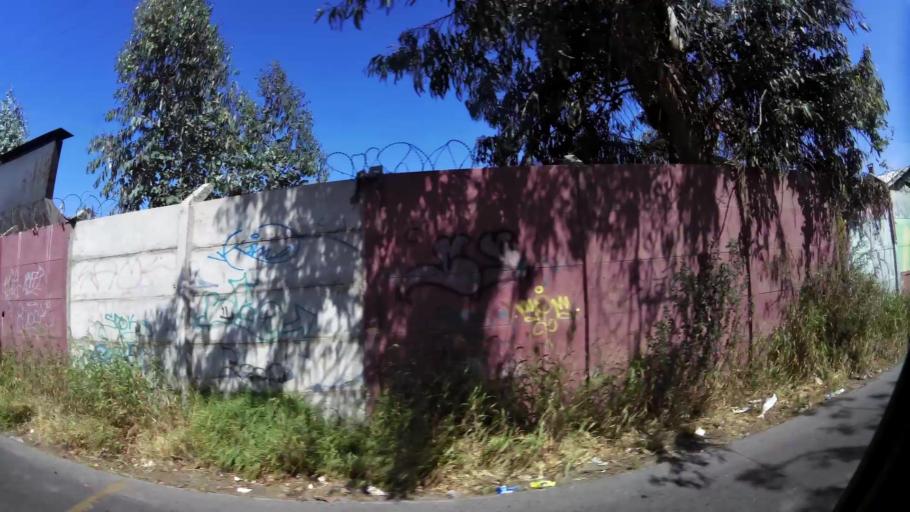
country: CL
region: Santiago Metropolitan
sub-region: Provincia de Santiago
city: Lo Prado
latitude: -33.5187
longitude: -70.7509
